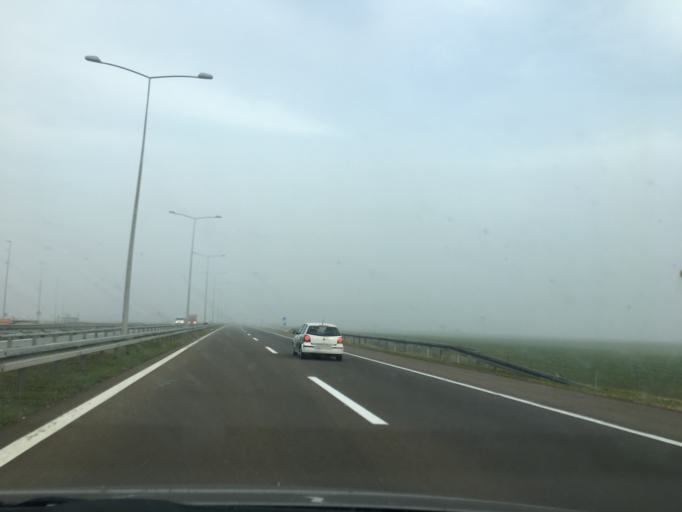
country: RS
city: Krcedin
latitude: 45.0948
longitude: 20.1201
